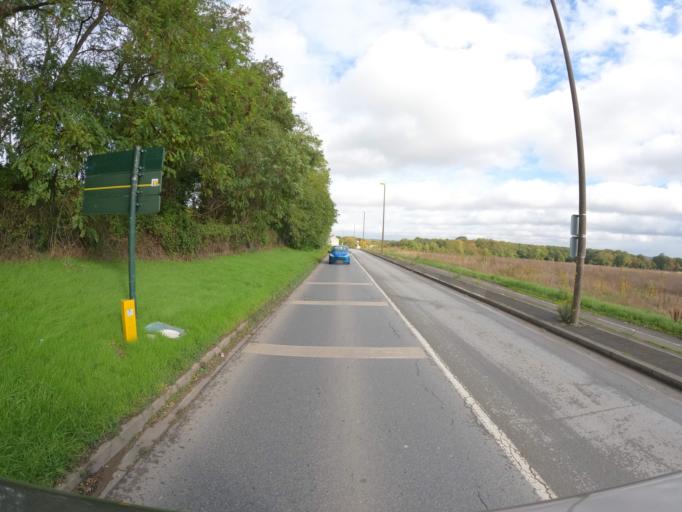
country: FR
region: Ile-de-France
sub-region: Departement de Seine-et-Marne
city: Chelles
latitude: 48.8934
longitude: 2.5907
